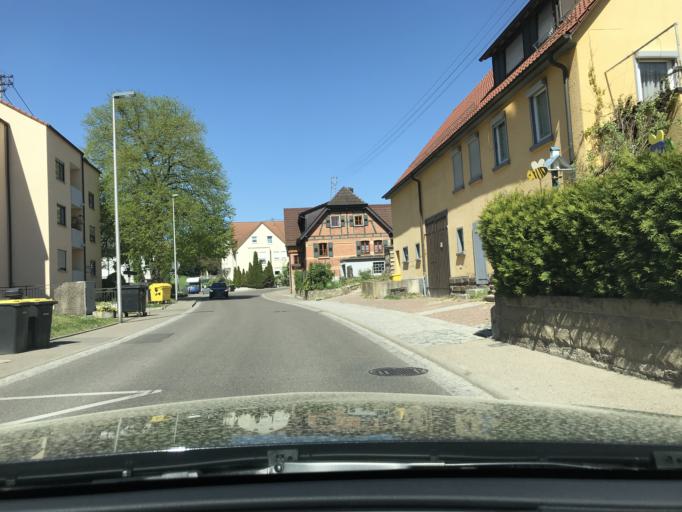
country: DE
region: Baden-Wuerttemberg
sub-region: Regierungsbezirk Stuttgart
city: Korb
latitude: 48.8296
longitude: 9.3743
